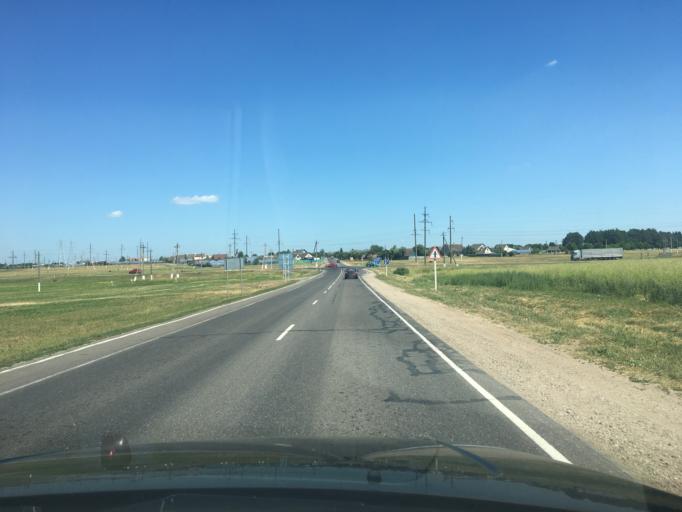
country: BY
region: Grodnenskaya
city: Iwye
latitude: 53.9136
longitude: 25.7649
